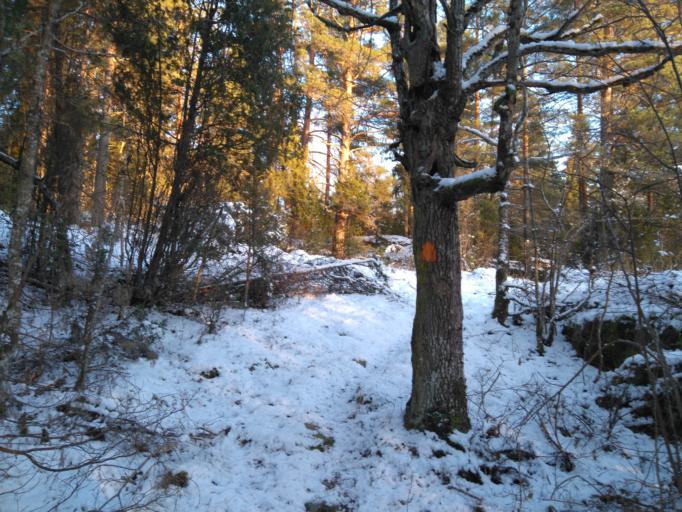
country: SE
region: Kalmar
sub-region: Vasterviks Kommun
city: Overum
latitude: 57.9080
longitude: 16.1290
